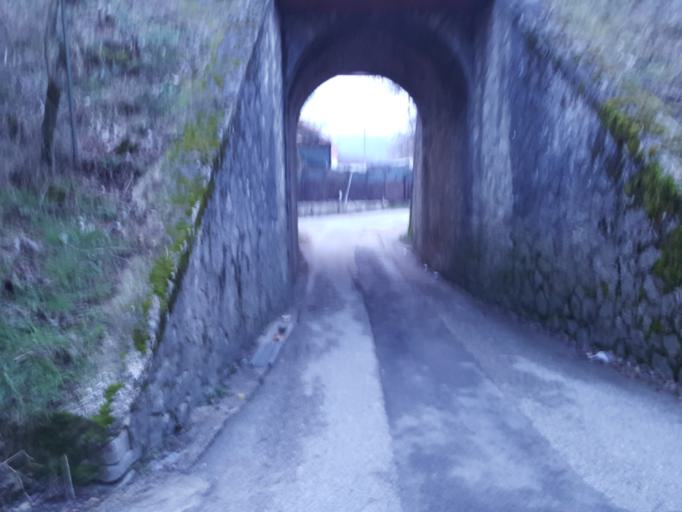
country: IT
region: Abruzzo
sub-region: Provincia dell' Aquila
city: Carsoli
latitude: 42.0889
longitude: 13.0634
